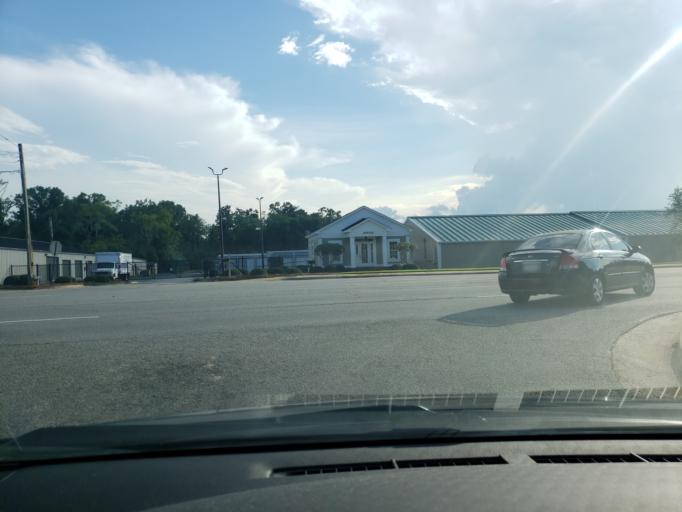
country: US
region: Georgia
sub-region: Dougherty County
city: Albany
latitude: 31.5845
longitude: -84.2048
